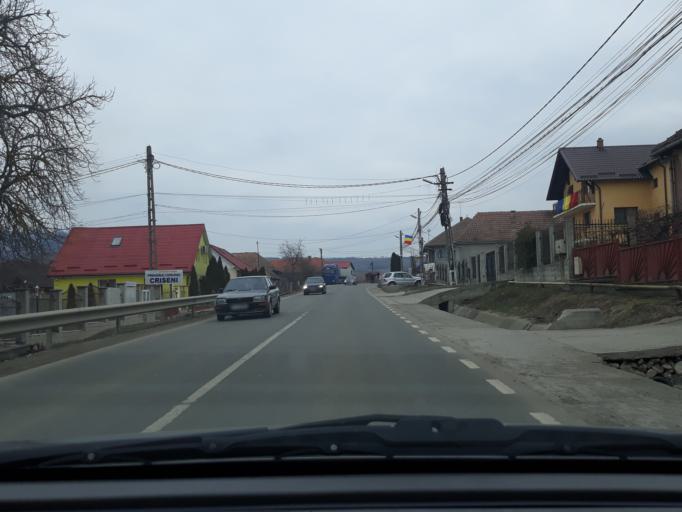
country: RO
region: Salaj
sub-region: Comuna Criseni
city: Criseni
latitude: 47.2315
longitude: 23.0453
